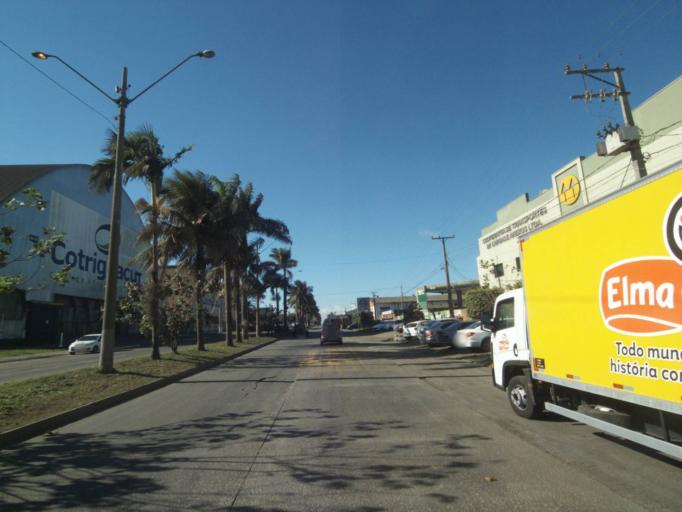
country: BR
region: Parana
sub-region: Paranagua
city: Paranagua
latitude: -25.5078
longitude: -48.5141
